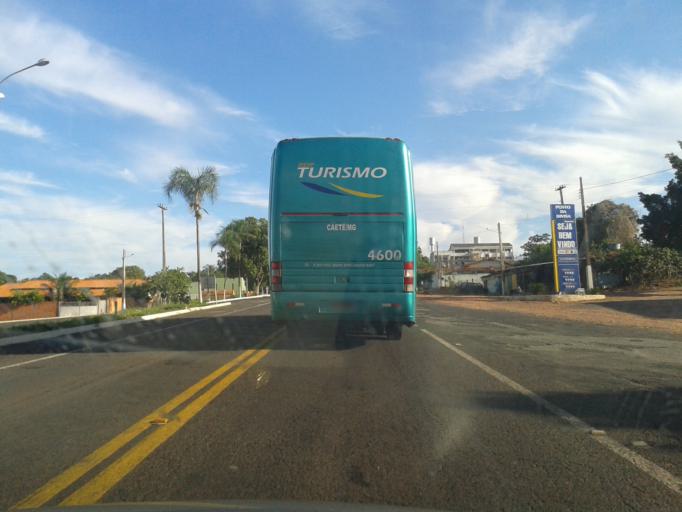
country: BR
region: Minas Gerais
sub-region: Tupaciguara
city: Tupaciguara
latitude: -18.3140
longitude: -48.5622
